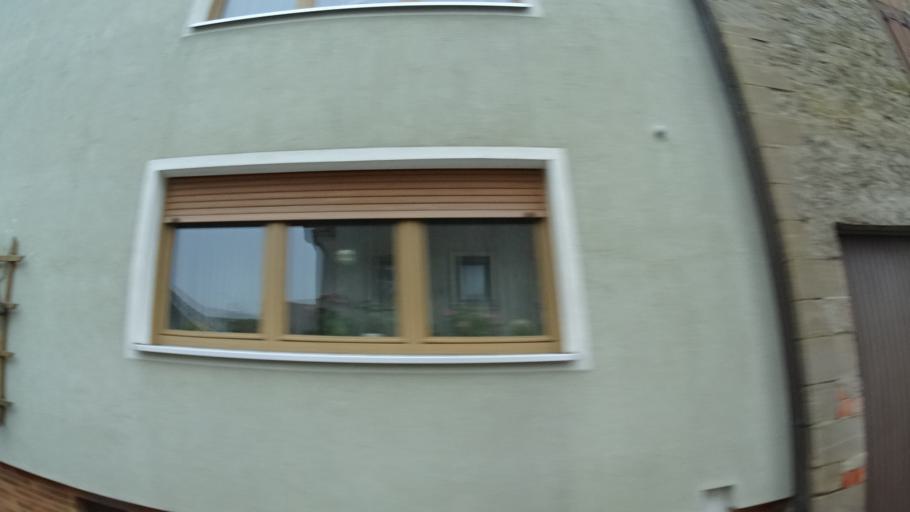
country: DE
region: Bavaria
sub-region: Regierungsbezirk Unterfranken
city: Donnersdorf
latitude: 49.9594
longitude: 10.4275
